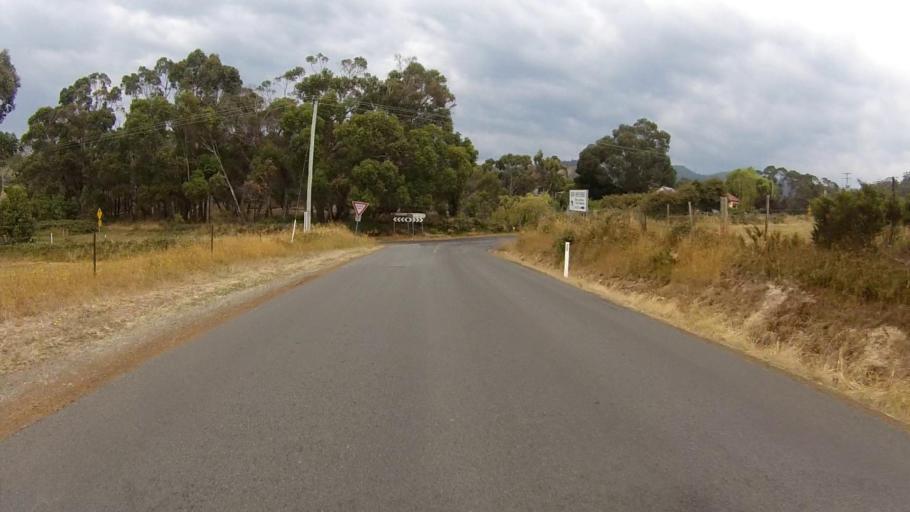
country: AU
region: Tasmania
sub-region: Huon Valley
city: Cygnet
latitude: -43.1843
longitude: 147.1079
